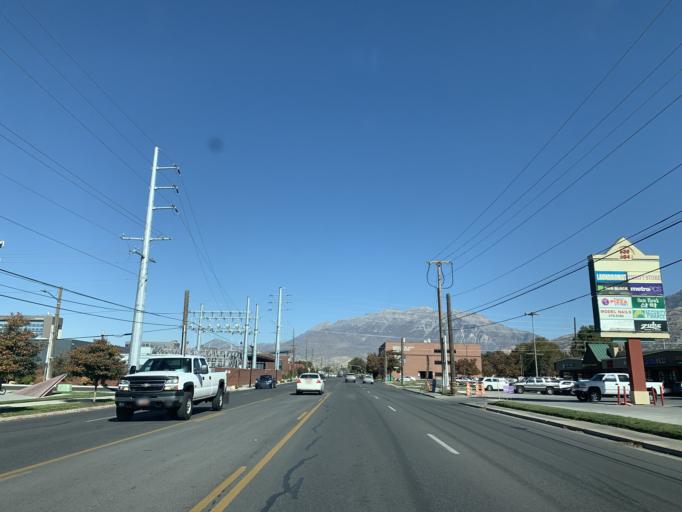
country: US
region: Utah
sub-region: Utah County
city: Provo
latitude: 40.2420
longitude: -111.6621
